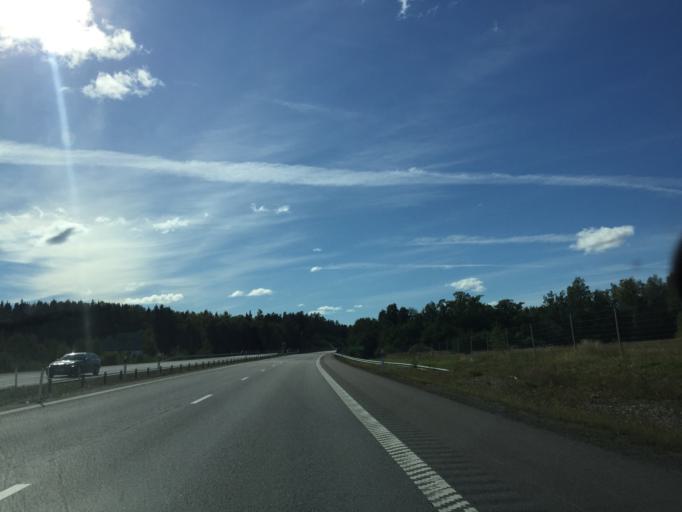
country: SE
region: Vaestmanland
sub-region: Arboga Kommun
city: Arboga
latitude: 59.4080
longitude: 15.7623
